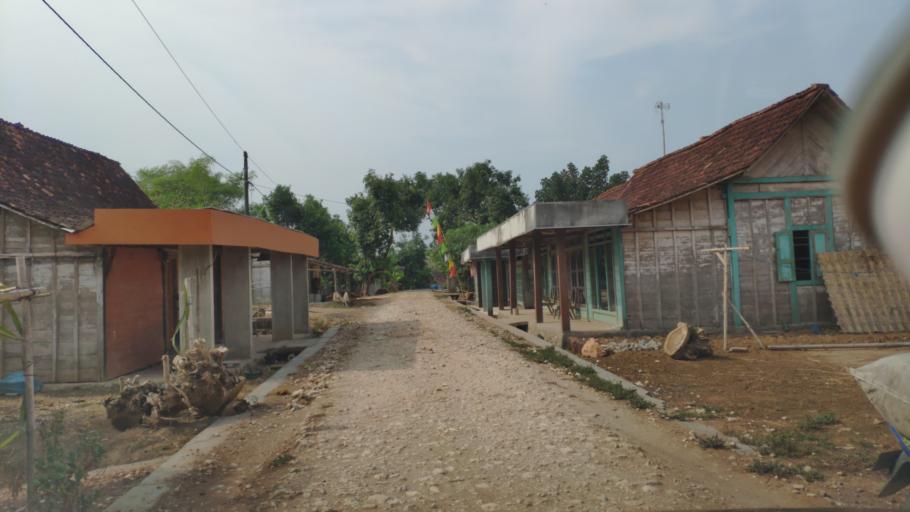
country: ID
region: Central Java
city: Tawangsari
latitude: -6.9658
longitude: 111.3444
